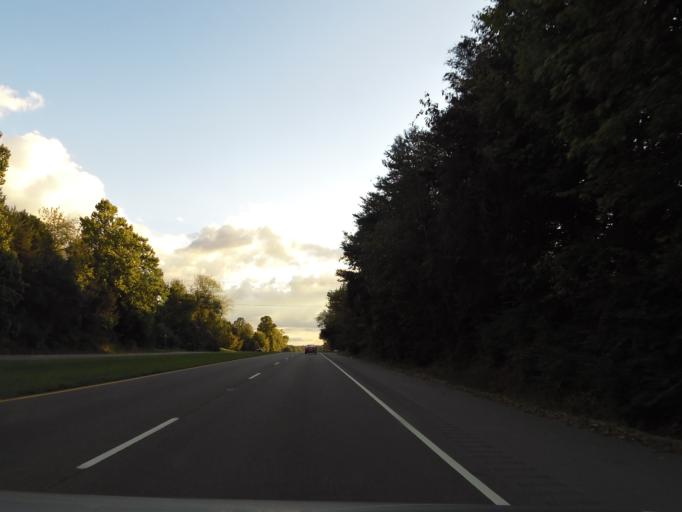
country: US
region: Tennessee
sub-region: Knox County
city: Mascot
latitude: 36.0426
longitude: -83.7160
